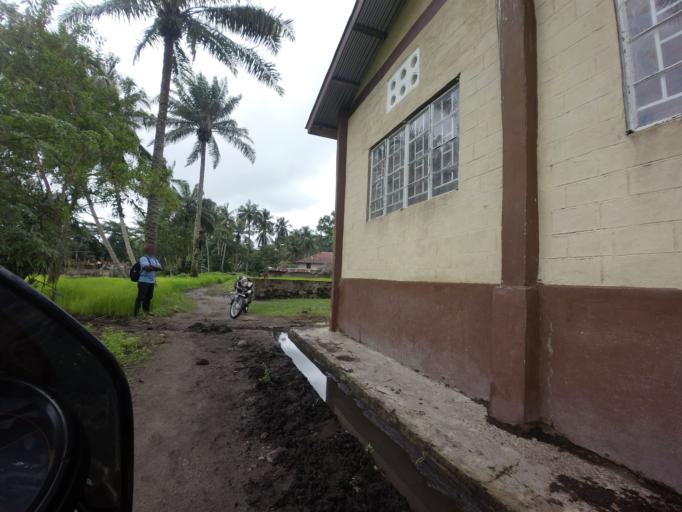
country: SL
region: Northern Province
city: Mambolo
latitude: 8.9756
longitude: -12.9955
